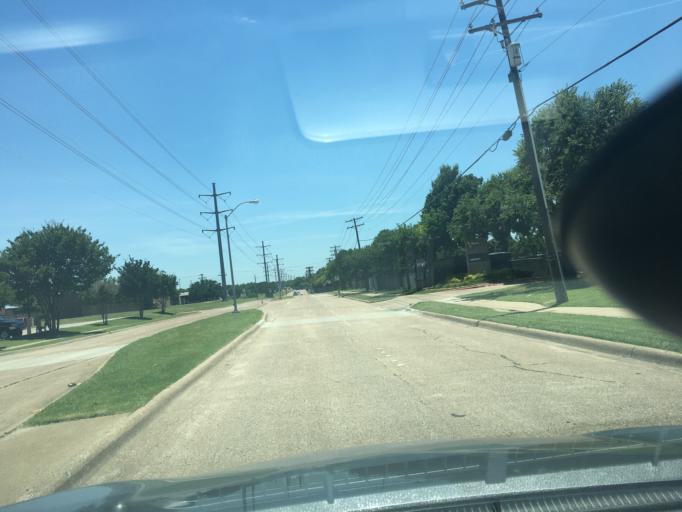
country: US
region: Texas
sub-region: Dallas County
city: Richardson
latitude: 32.9552
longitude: -96.7053
